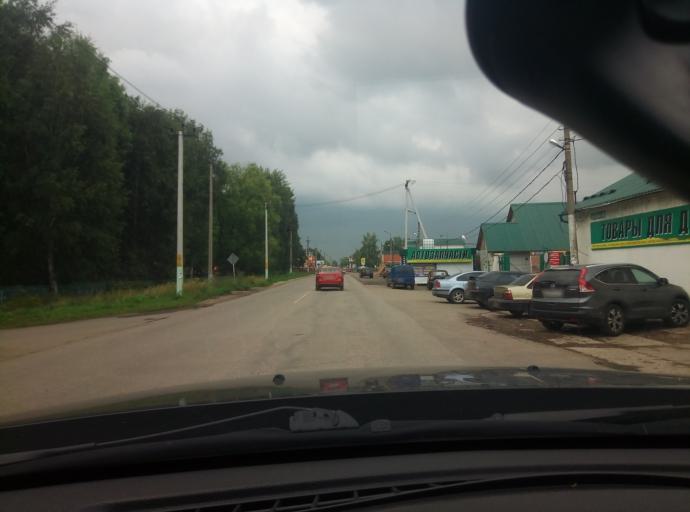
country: RU
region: Tula
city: Kimovsk
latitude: 53.9674
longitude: 38.5408
